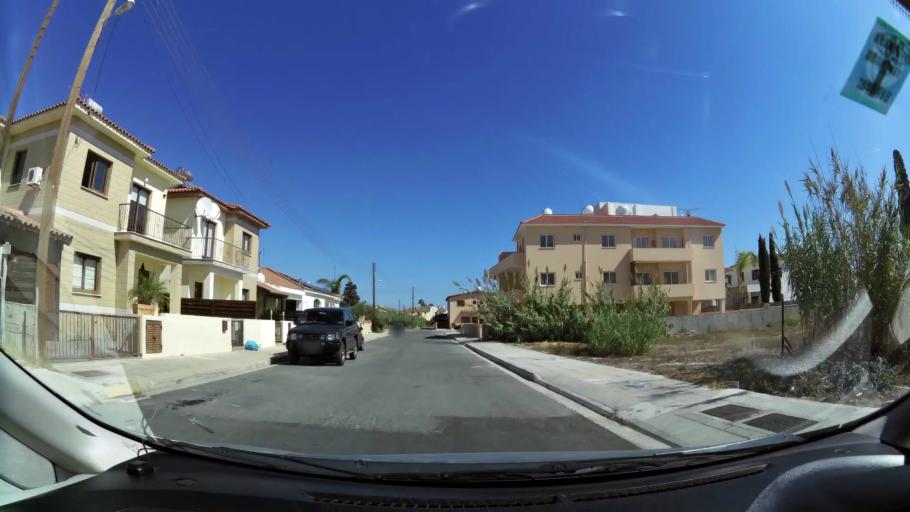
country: CY
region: Larnaka
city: Livadia
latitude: 34.9591
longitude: 33.6253
